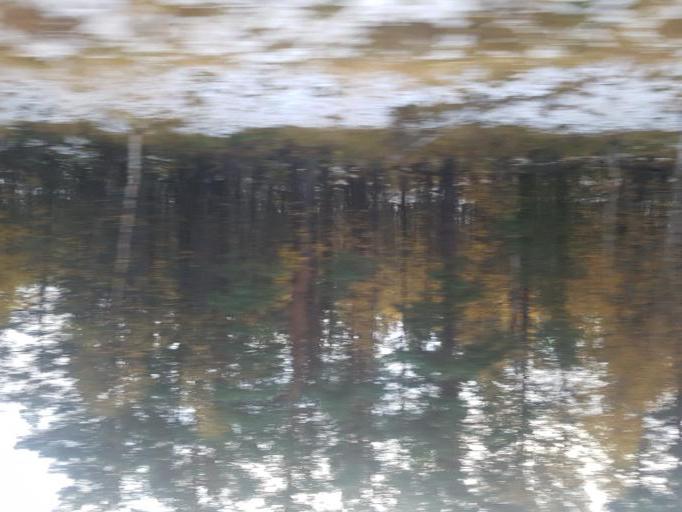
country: NO
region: Sor-Trondelag
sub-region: Oppdal
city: Oppdal
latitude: 62.6345
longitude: 9.7968
